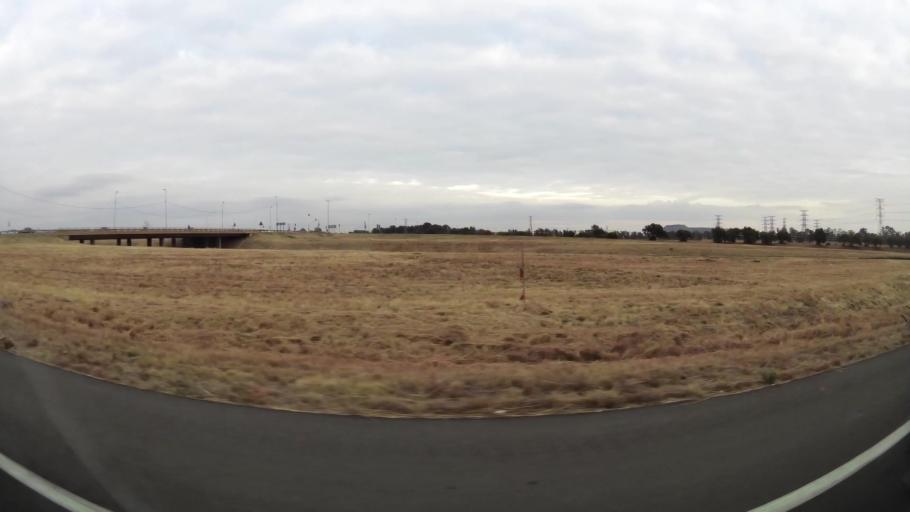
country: ZA
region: Orange Free State
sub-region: Mangaung Metropolitan Municipality
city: Bloemfontein
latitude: -29.1261
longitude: 26.1642
